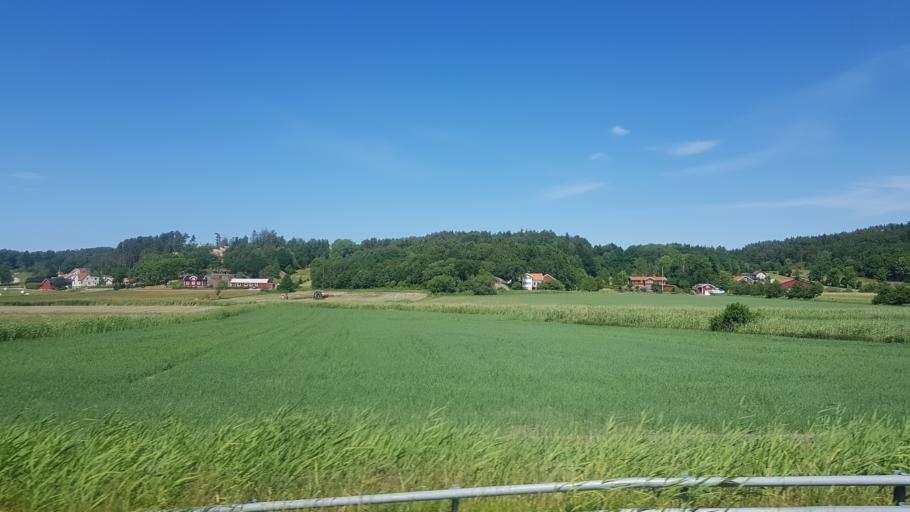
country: SE
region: Vaestra Goetaland
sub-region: Tjorns Kommun
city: Skaerhamn
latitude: 58.0212
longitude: 11.6217
